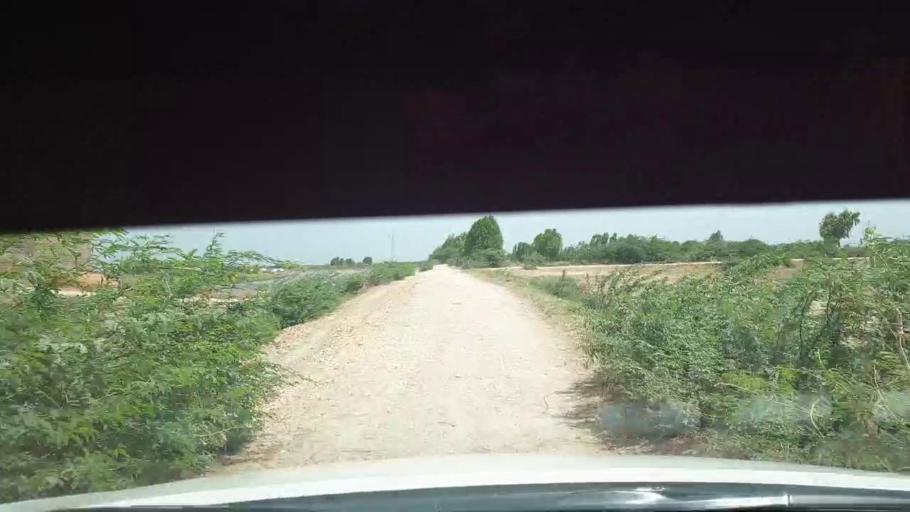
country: PK
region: Sindh
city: Kadhan
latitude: 24.4893
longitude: 68.9831
